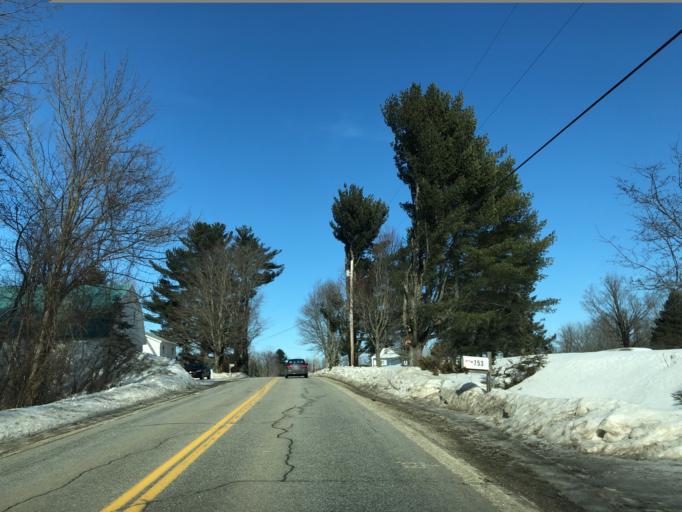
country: US
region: Maine
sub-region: Oxford County
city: Hebron
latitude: 44.2213
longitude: -70.3395
